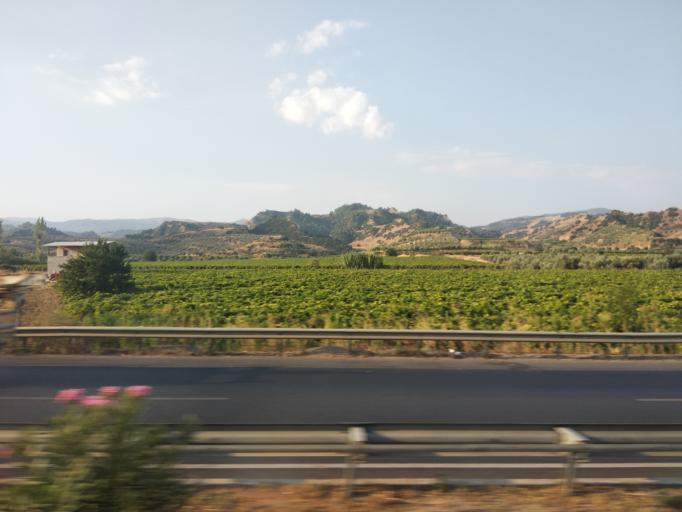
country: TR
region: Manisa
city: Ahmetli
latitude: 38.5069
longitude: 27.9933
